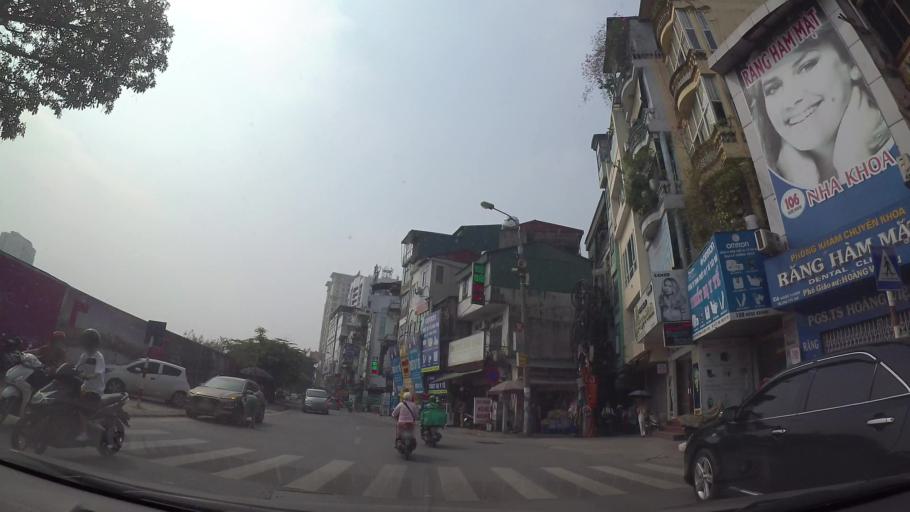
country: VN
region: Ha Noi
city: Dong Da
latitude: 21.0263
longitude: 105.8178
